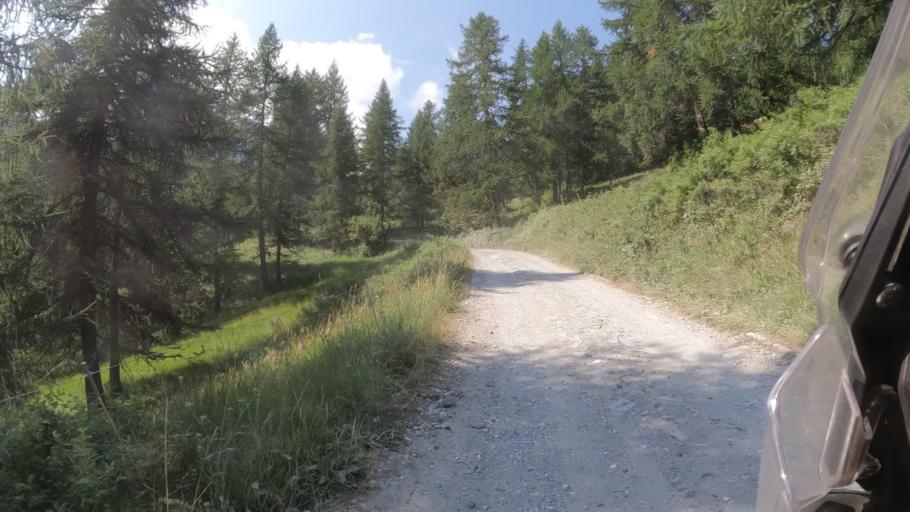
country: IT
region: Piedmont
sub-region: Provincia di Torino
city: Cesana Torinese
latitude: 44.9214
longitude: 6.8063
